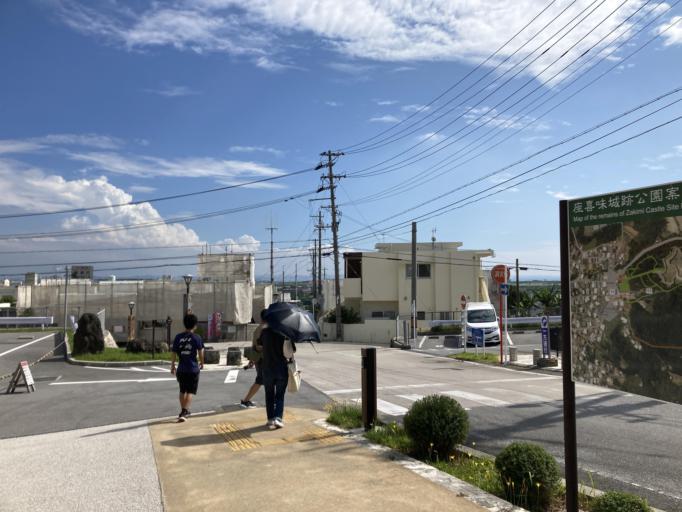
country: JP
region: Okinawa
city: Ishikawa
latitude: 26.4067
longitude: 127.7422
